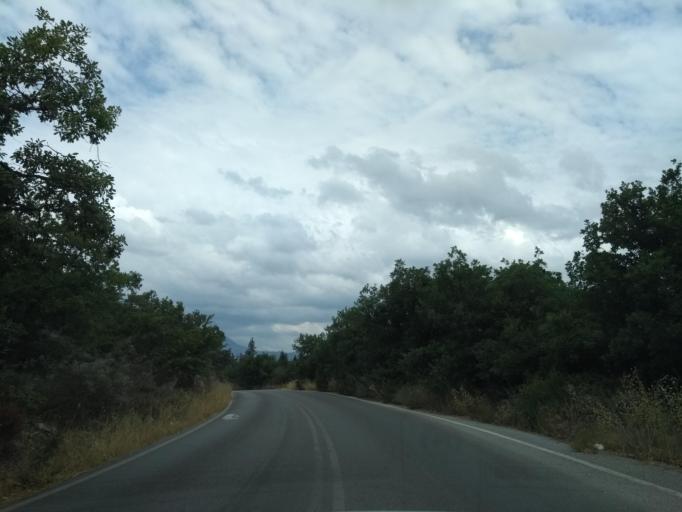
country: GR
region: Crete
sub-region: Nomos Chanias
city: Kalivai
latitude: 35.4091
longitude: 24.2086
